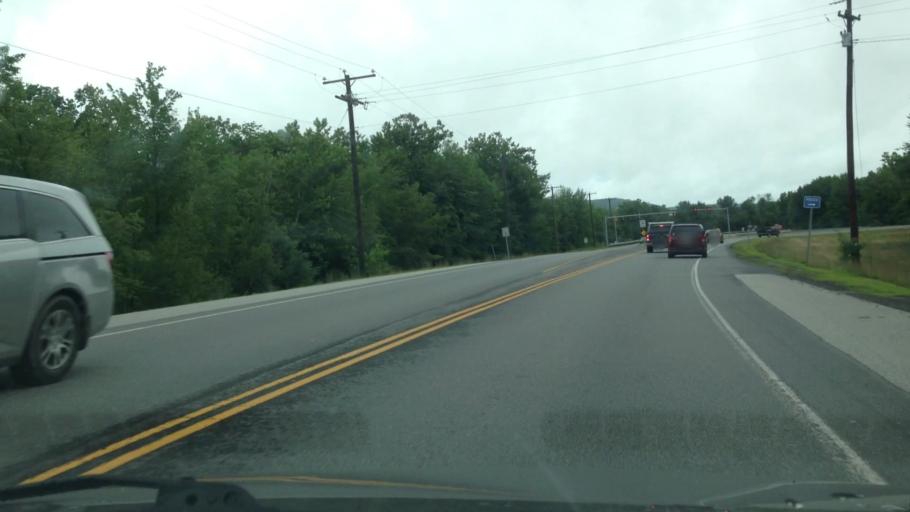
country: US
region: New Hampshire
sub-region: Cheshire County
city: Keene
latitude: 42.9152
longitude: -72.2605
